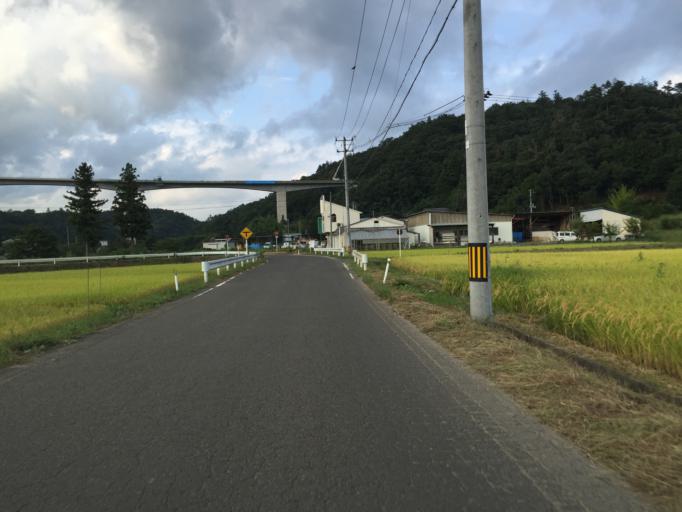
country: JP
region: Fukushima
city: Hobaramachi
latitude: 37.7557
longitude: 140.6108
